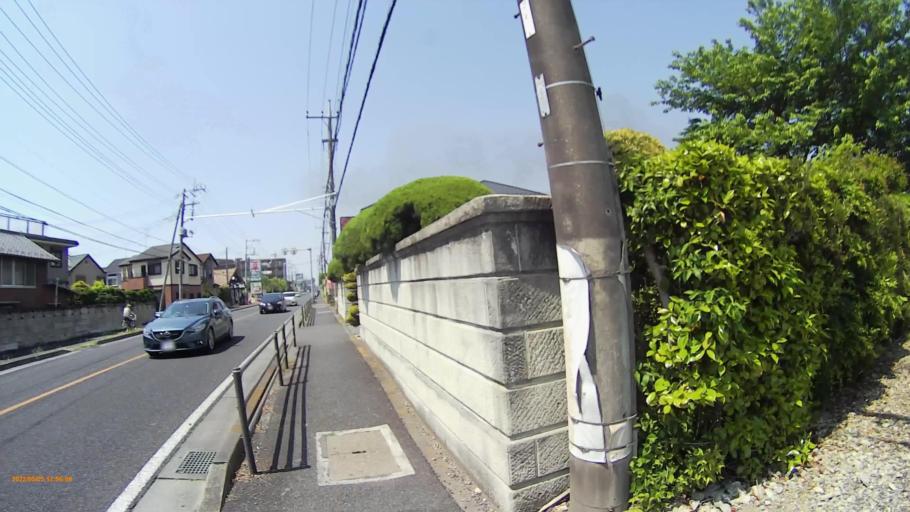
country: JP
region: Saitama
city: Kasukabe
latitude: 35.9575
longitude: 139.7756
